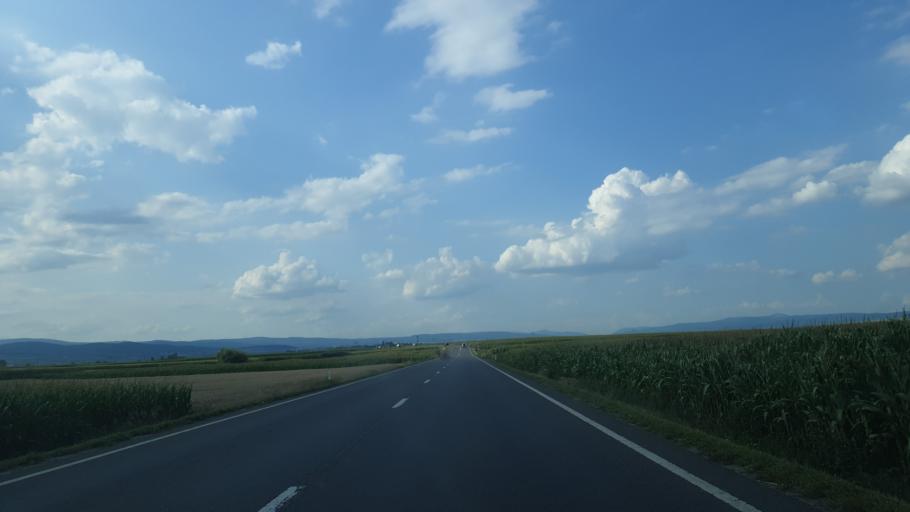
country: RO
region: Covasna
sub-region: Comuna Chichis
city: Chichis
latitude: 45.7881
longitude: 25.8070
